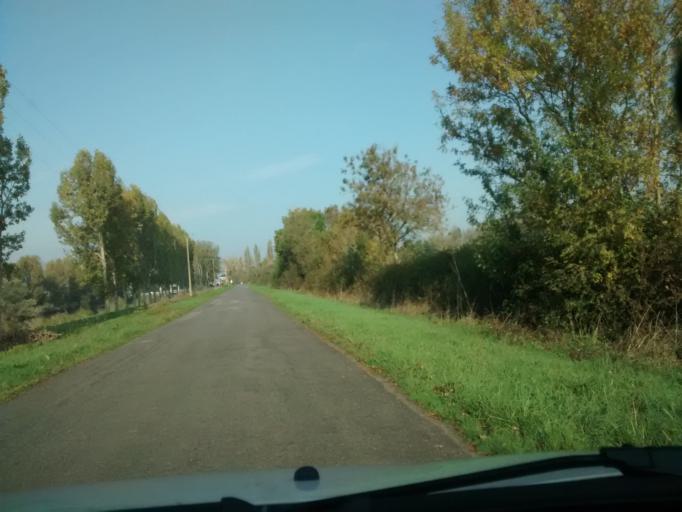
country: FR
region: Pays de la Loire
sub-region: Departement de la Loire-Atlantique
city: Vue
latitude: 47.2362
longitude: -1.8660
